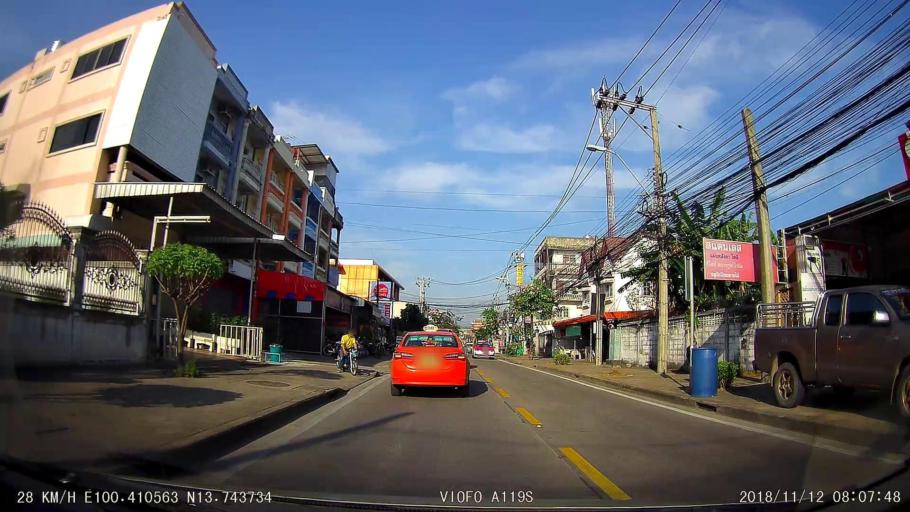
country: TH
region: Bangkok
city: Phasi Charoen
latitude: 13.7438
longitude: 100.4104
